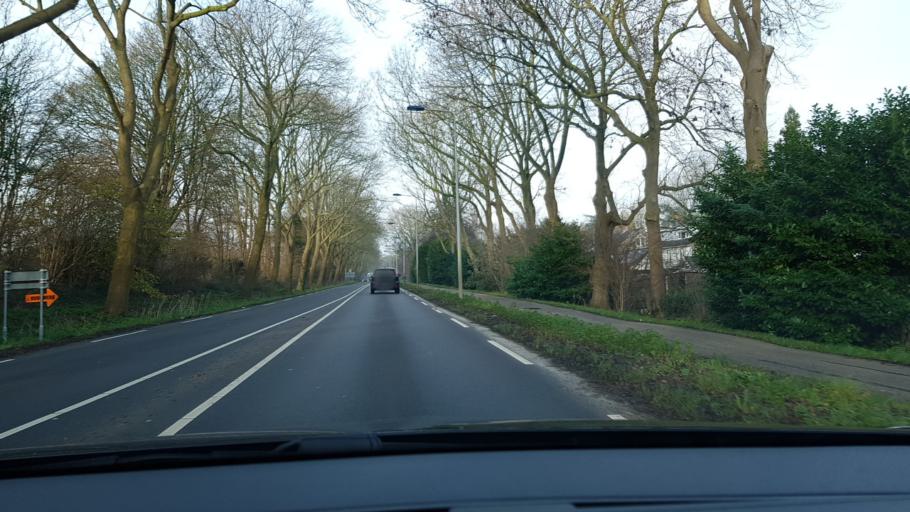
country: NL
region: North Holland
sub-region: Gemeente Uithoorn
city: Uithoorn
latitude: 52.2342
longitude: 4.8279
